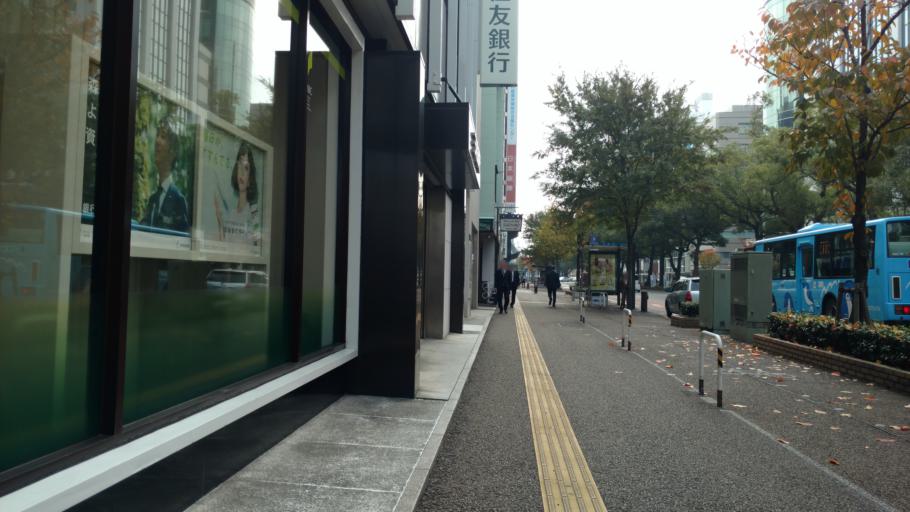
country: JP
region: Kagawa
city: Takamatsu-shi
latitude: 34.3463
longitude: 134.0485
